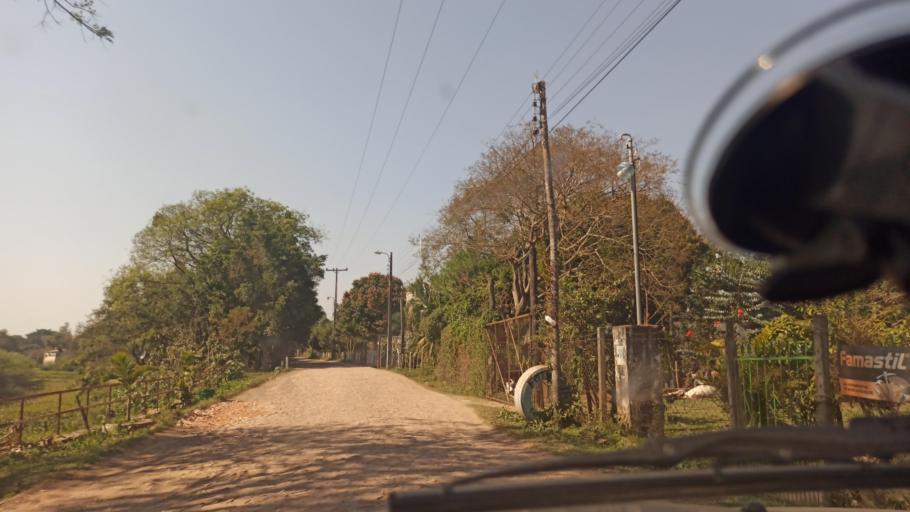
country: AR
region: Formosa
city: Clorinda
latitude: -25.2954
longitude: -57.7001
